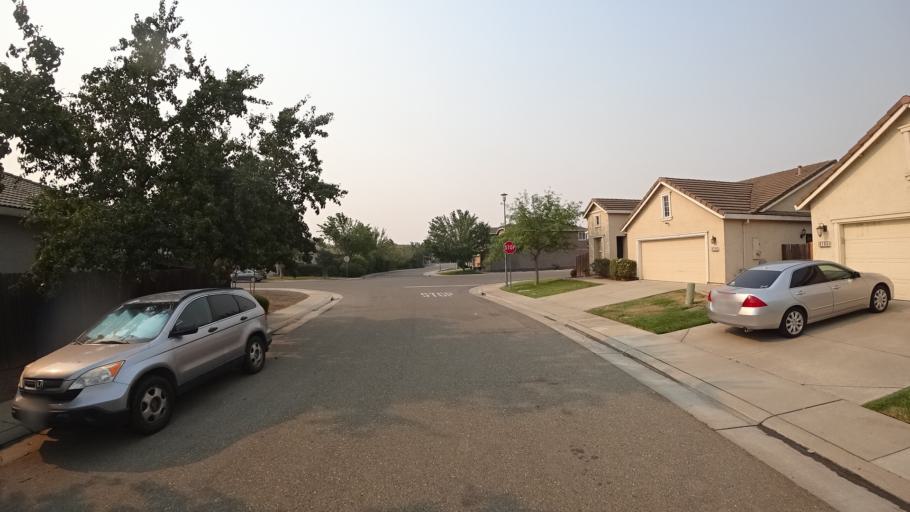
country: US
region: California
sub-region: Sacramento County
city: Laguna
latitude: 38.4012
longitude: -121.4501
